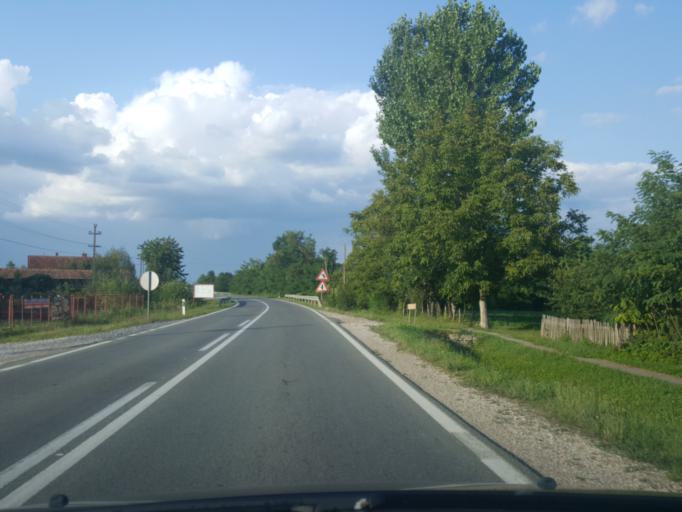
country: RS
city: Lipnicki Sor
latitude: 44.6097
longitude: 19.2601
